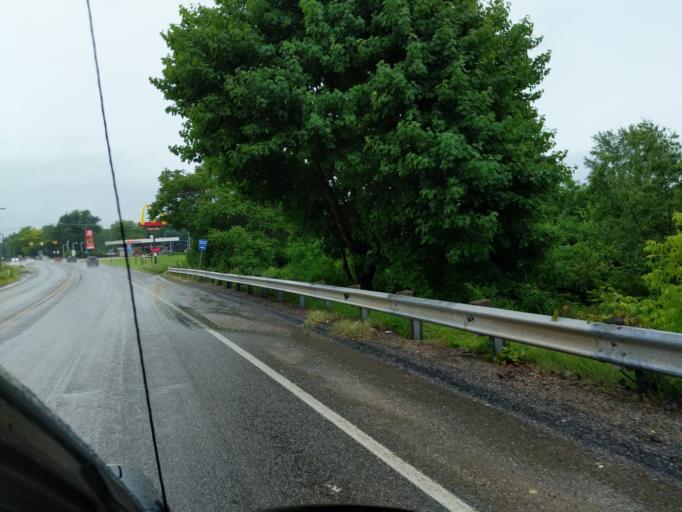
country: US
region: Michigan
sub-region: Berrien County
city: Coloma
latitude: 42.1772
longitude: -86.3045
